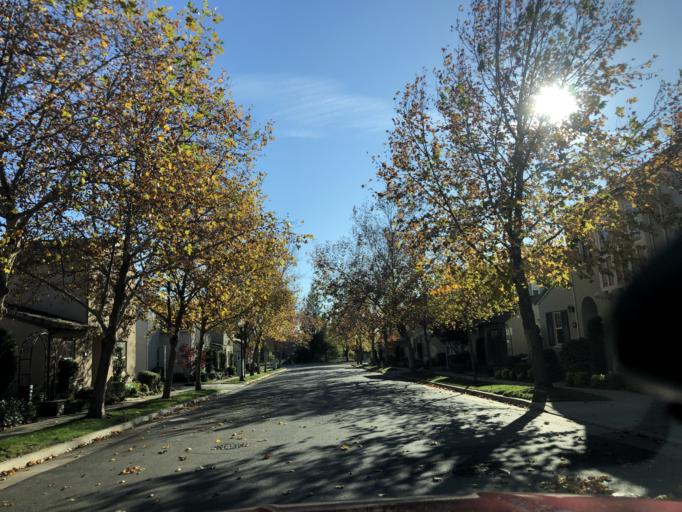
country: US
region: California
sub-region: Placer County
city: Roseville
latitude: 38.7828
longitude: -121.2879
